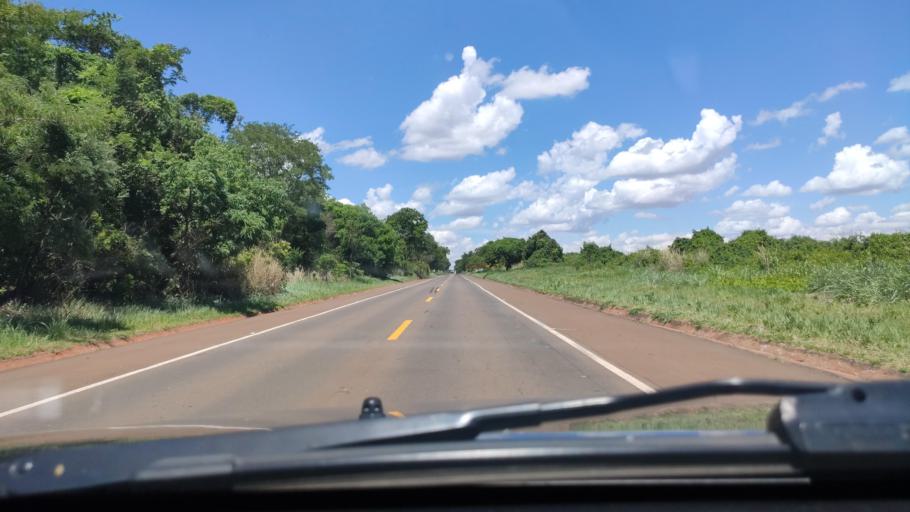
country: BR
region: Sao Paulo
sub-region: Boa Esperanca Do Sul
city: Boa Esperanca do Sul
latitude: -22.0693
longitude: -48.3902
